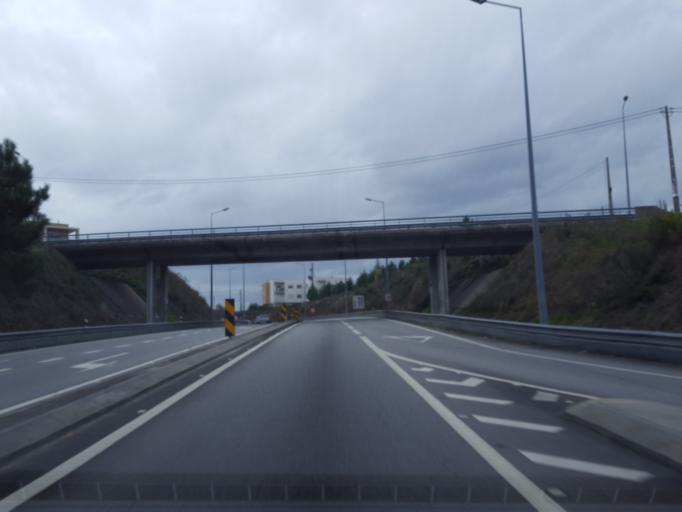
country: PT
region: Porto
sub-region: Marco de Canaveses
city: Marco de Canavezes
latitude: 41.2092
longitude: -8.1658
